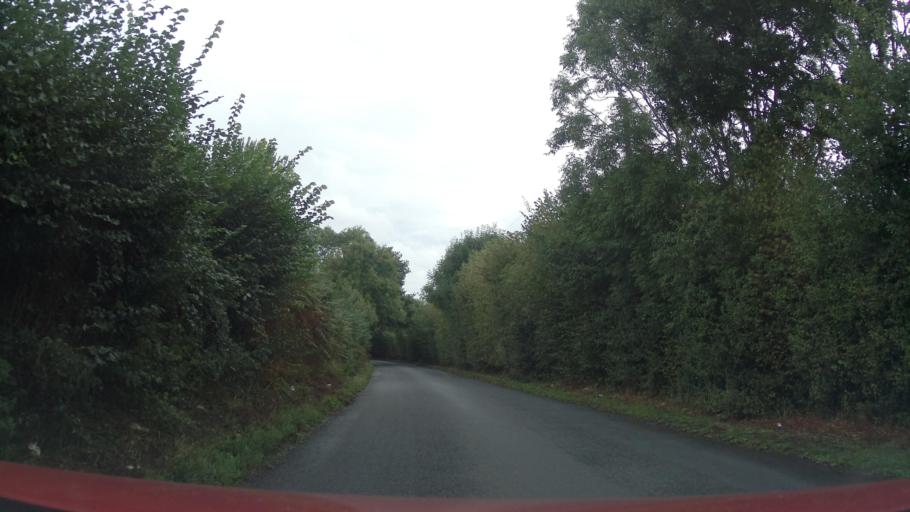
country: GB
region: England
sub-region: Worcestershire
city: Kidderminster
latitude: 52.3521
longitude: -2.1927
